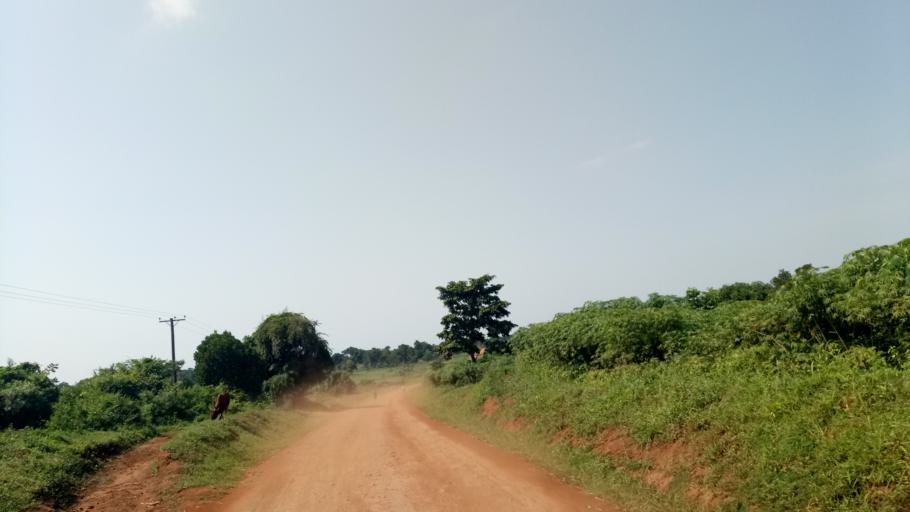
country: UG
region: Eastern Region
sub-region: Kaliro District
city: Kaliro
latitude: 0.9760
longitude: 33.4596
